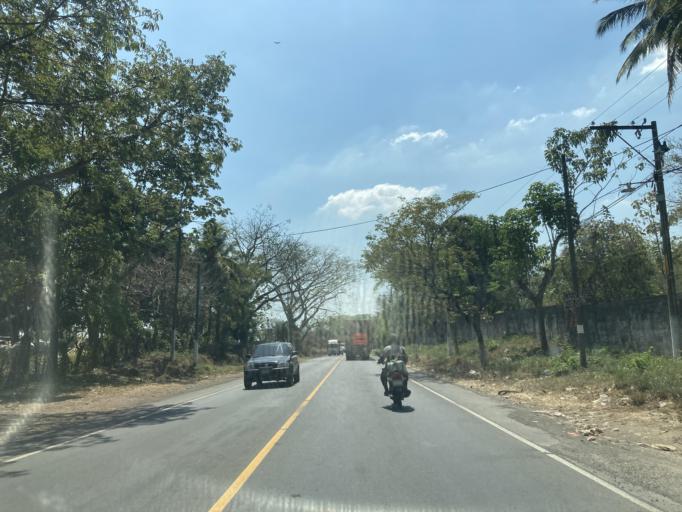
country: GT
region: Escuintla
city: Guanagazapa
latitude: 14.2161
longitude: -90.7247
